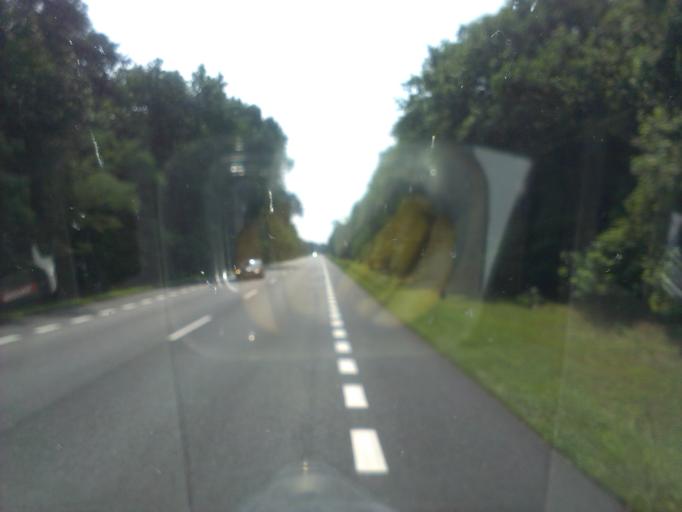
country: PL
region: Lubusz
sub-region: Powiat nowosolski
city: Nowe Miasteczko
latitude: 51.7149
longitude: 15.7294
